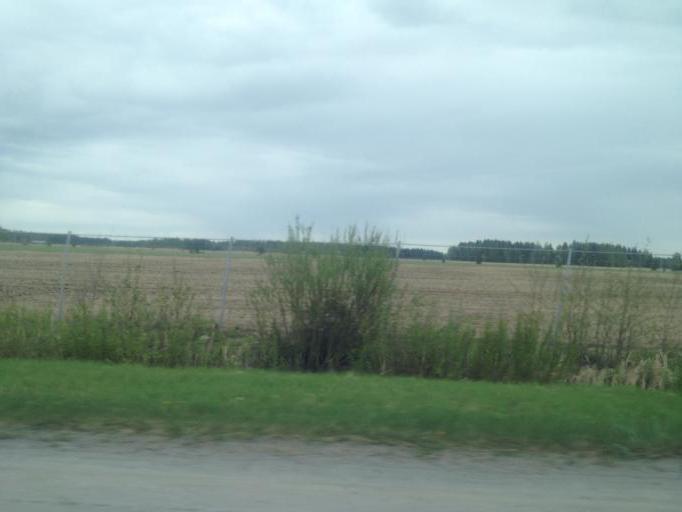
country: FI
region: Uusimaa
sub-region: Helsinki
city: Nurmijaervi
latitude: 60.5214
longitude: 24.8454
